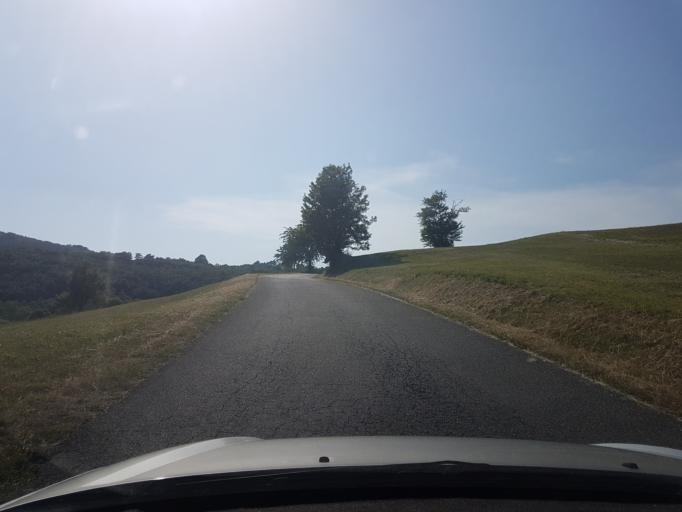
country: SI
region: Divaca
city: Divaca
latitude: 45.7607
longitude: 13.9851
